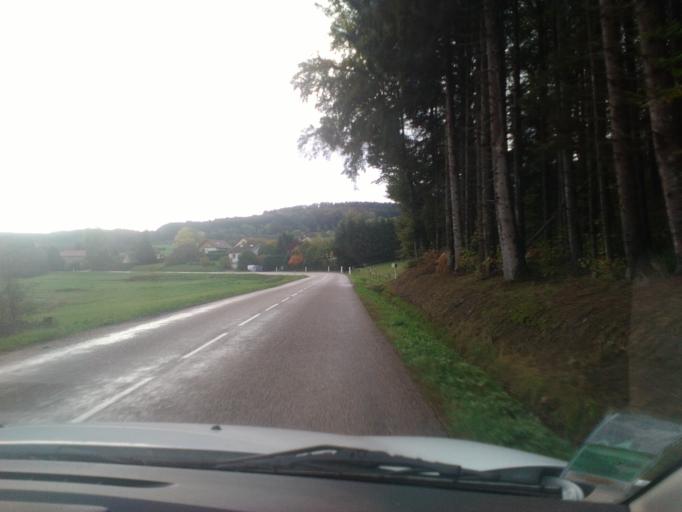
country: FR
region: Lorraine
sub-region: Departement des Vosges
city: Granges-sur-Vologne
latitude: 48.1837
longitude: 6.7984
